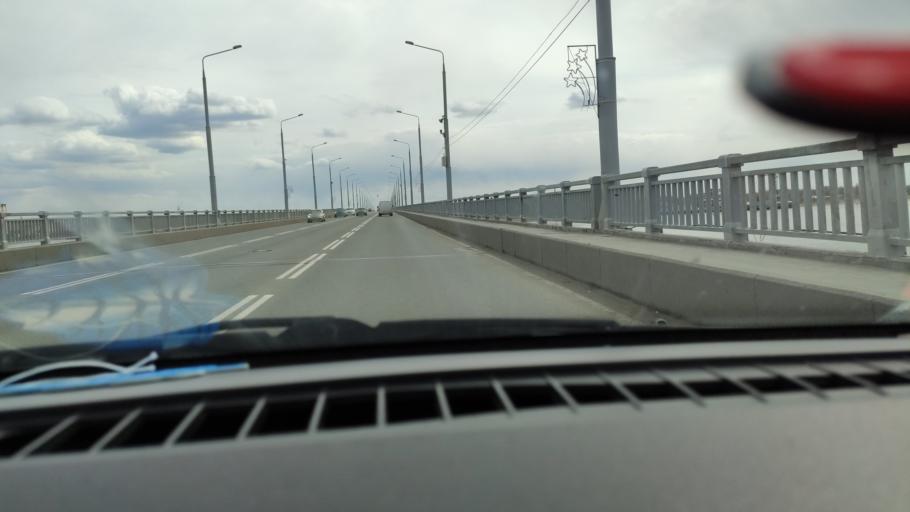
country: RU
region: Saratov
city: Engel's
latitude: 51.5092
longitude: 46.0760
